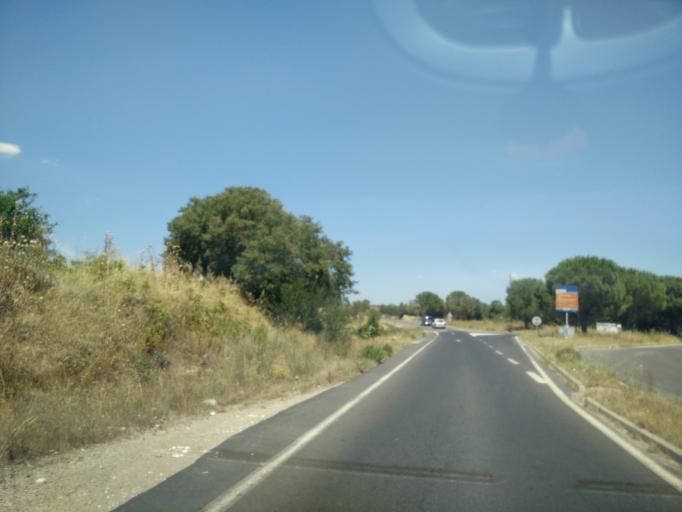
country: FR
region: Languedoc-Roussillon
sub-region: Departement de l'Herault
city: Lunel
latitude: 43.6990
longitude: 4.1291
